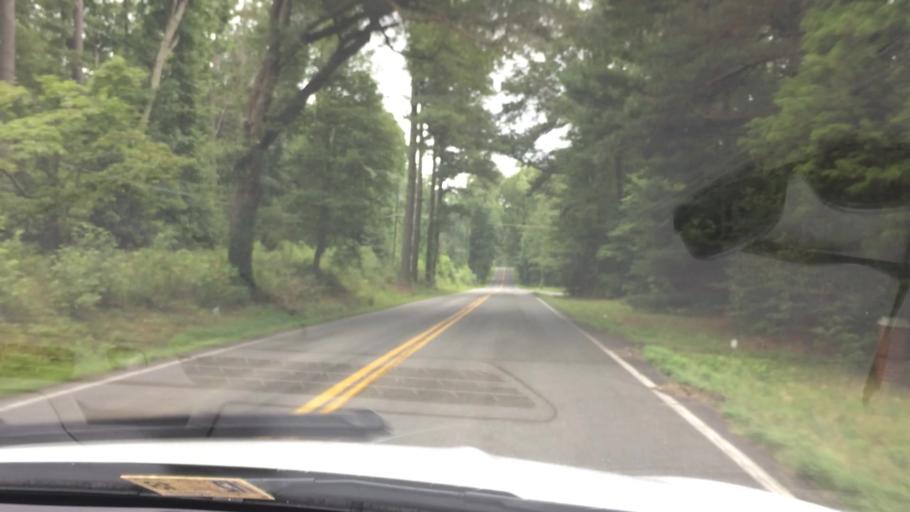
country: US
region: Virginia
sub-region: Charles City County
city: Charles City
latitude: 37.4100
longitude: -77.0459
